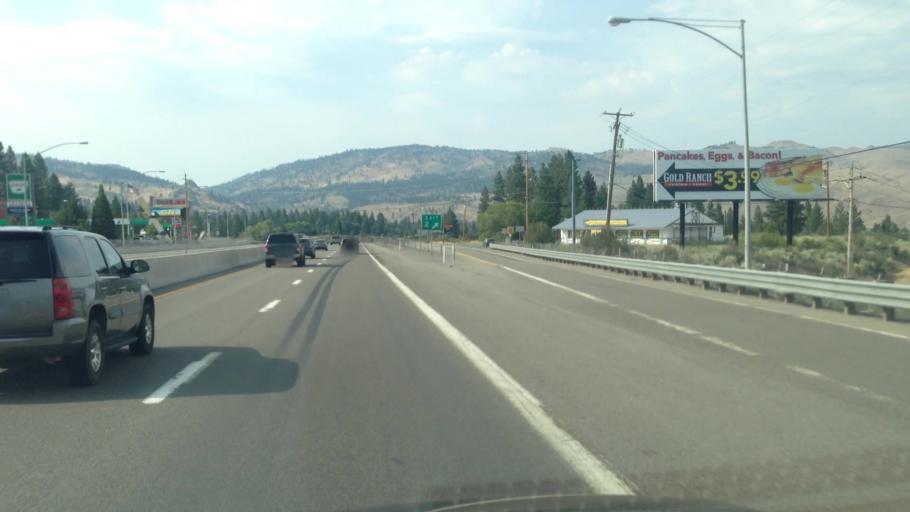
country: US
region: Nevada
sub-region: Washoe County
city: Verdi
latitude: 39.5000
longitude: -119.9988
